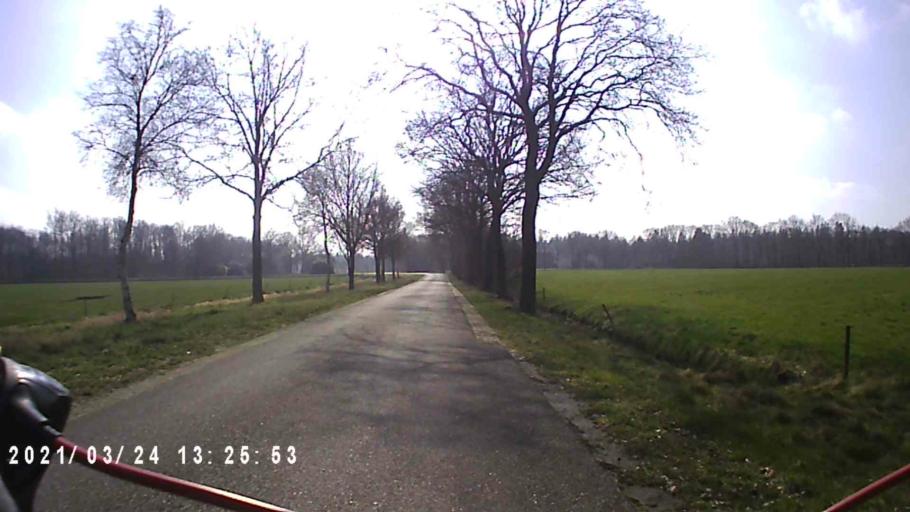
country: NL
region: Groningen
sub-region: Gemeente Leek
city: Leek
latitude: 53.0921
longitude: 6.2793
